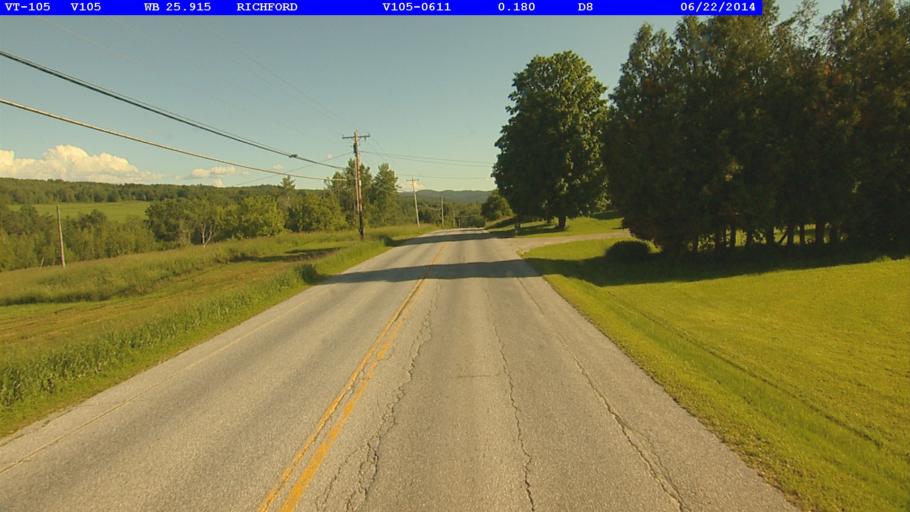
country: US
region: Vermont
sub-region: Franklin County
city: Richford
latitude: 44.9739
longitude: -72.6884
